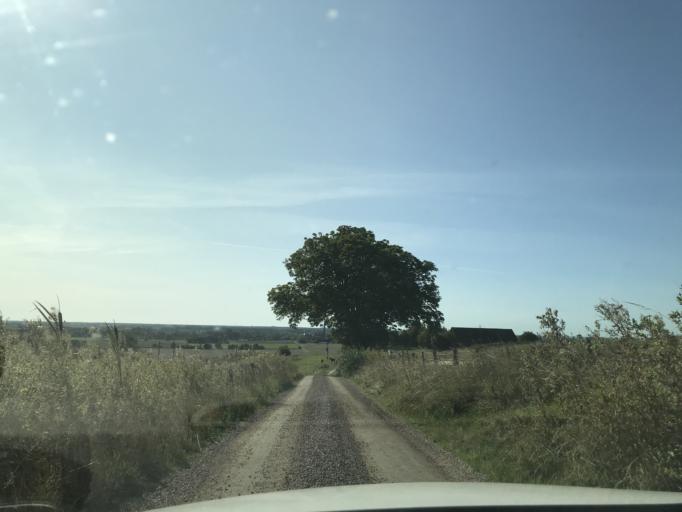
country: SE
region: Skane
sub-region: Landskrona
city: Asmundtorp
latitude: 55.9050
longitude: 12.9498
